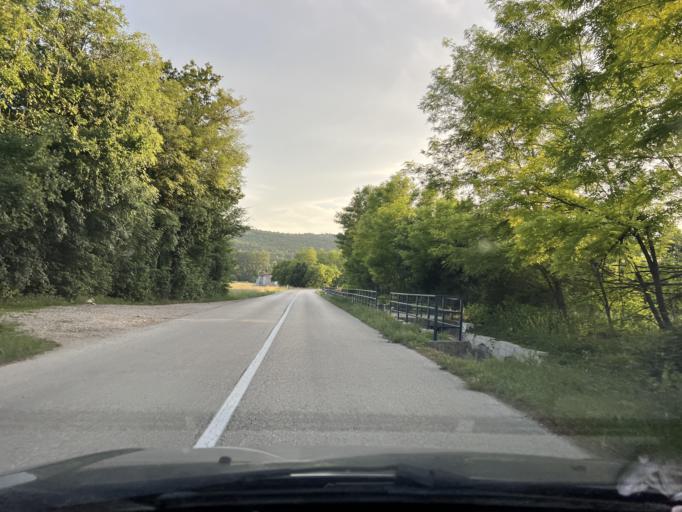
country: HR
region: Primorsko-Goranska
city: Podhum
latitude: 45.3757
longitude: 14.4802
